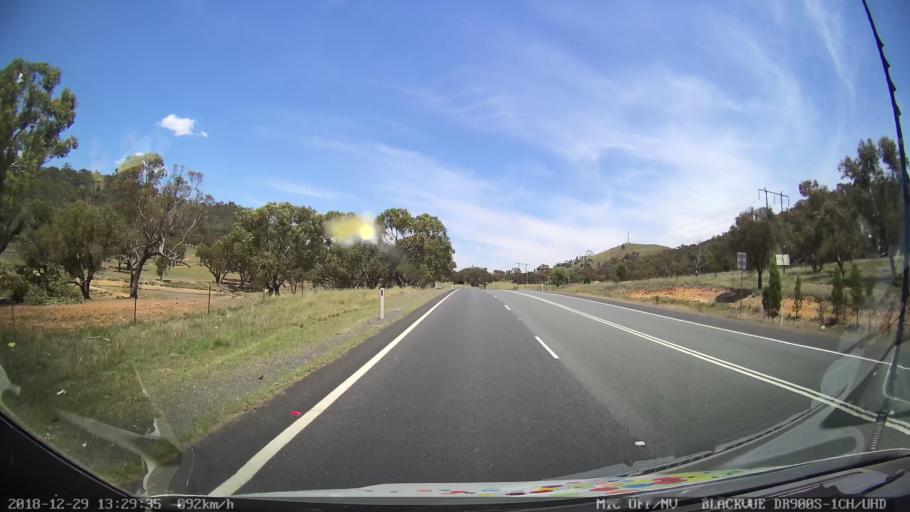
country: AU
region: New South Wales
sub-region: Cooma-Monaro
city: Cooma
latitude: -35.8922
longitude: 149.1614
